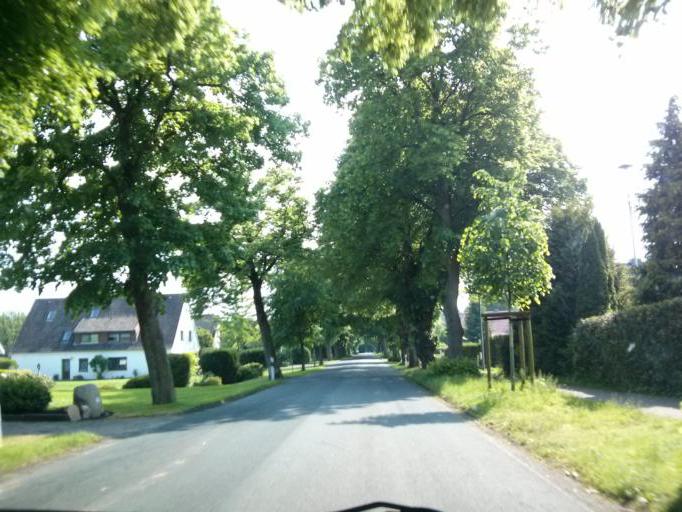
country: DE
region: Lower Saxony
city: Schiffdorf
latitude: 53.5127
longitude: 8.7214
